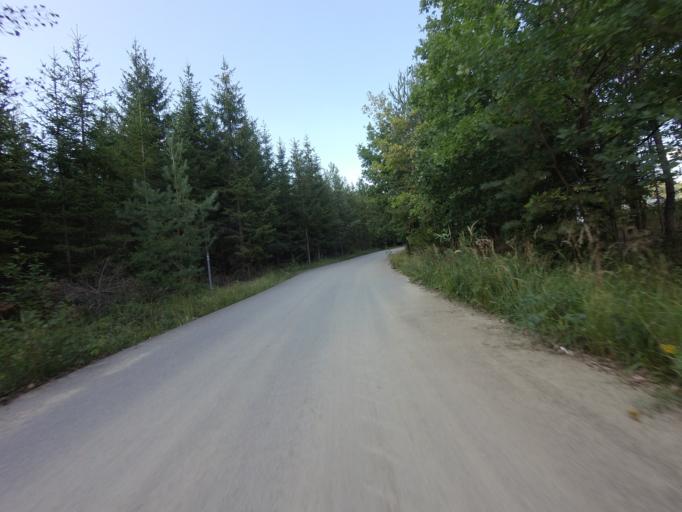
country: CZ
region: Jihocesky
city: Tyn nad Vltavou
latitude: 49.1793
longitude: 14.4430
